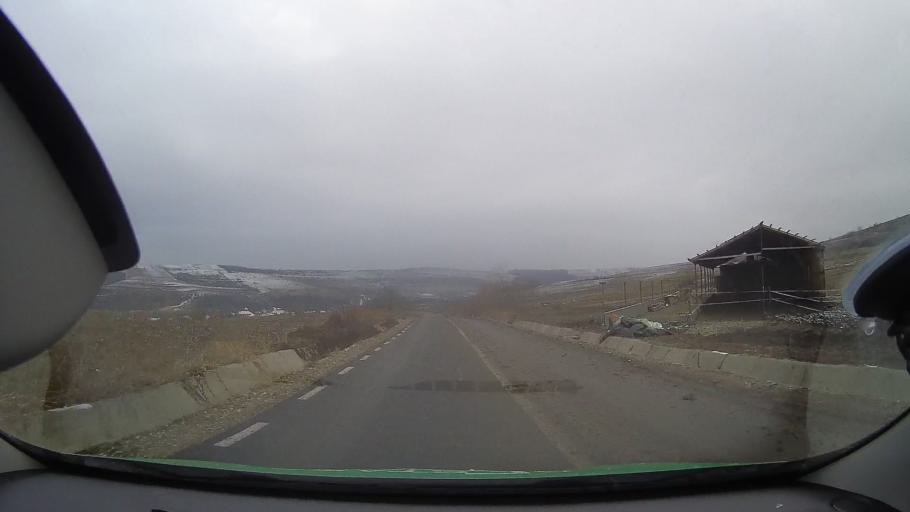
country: RO
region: Alba
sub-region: Comuna Farau
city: Farau
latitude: 46.3938
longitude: 24.0206
